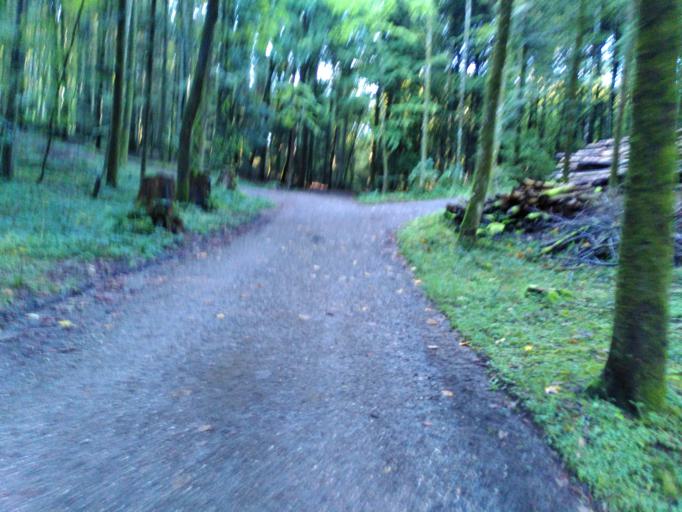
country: CH
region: Bern
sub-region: Emmental District
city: Ersigen
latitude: 47.0992
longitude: 7.6155
